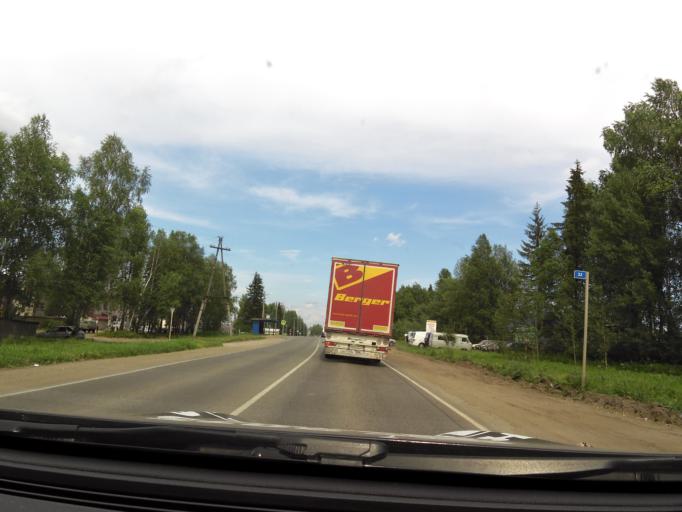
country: RU
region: Kirov
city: Stulovo
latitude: 58.7152
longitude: 50.1260
